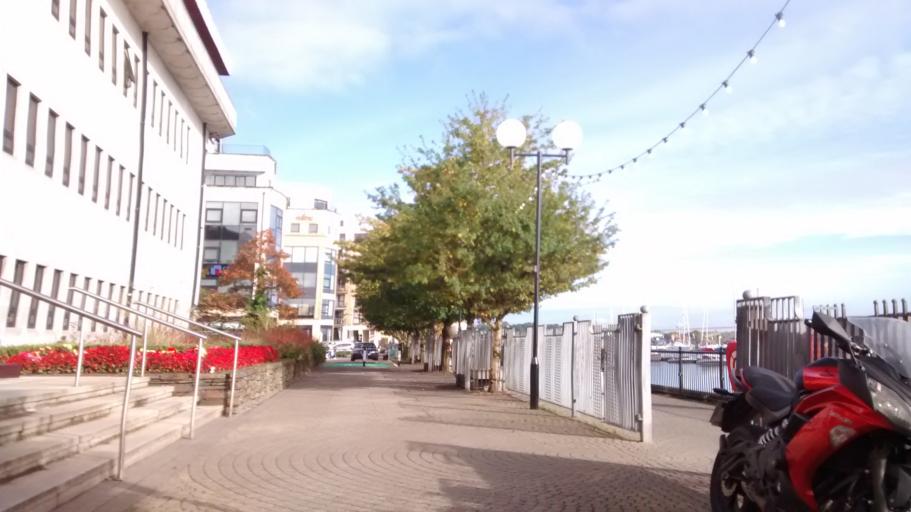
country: GB
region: Northern Ireland
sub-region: City of Derry
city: Derry
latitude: 55.0049
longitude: -7.3207
